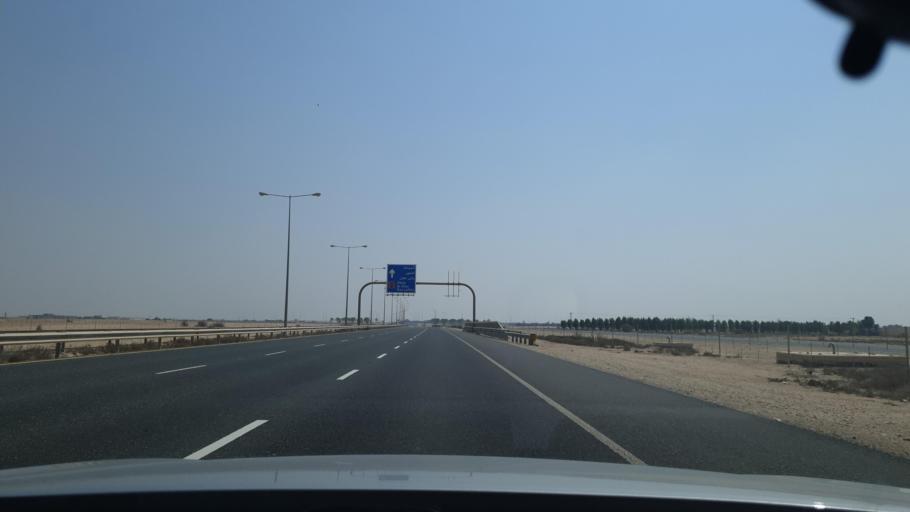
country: QA
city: Al Ghuwayriyah
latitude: 25.7929
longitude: 51.3893
